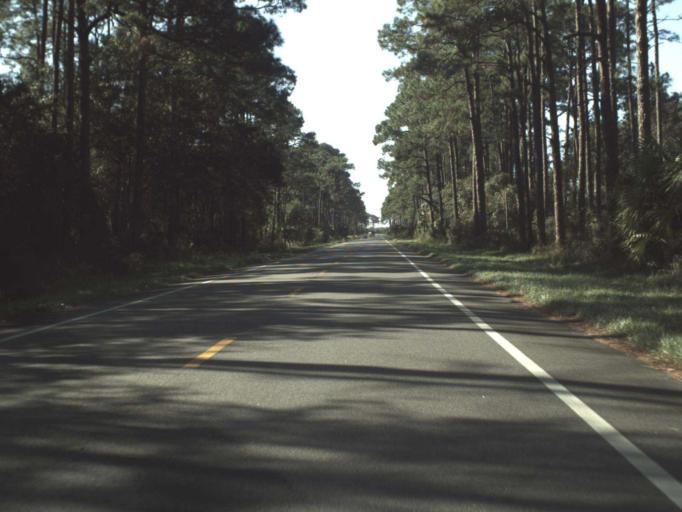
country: US
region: Florida
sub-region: Franklin County
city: Apalachicola
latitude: 29.7171
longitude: -85.0488
